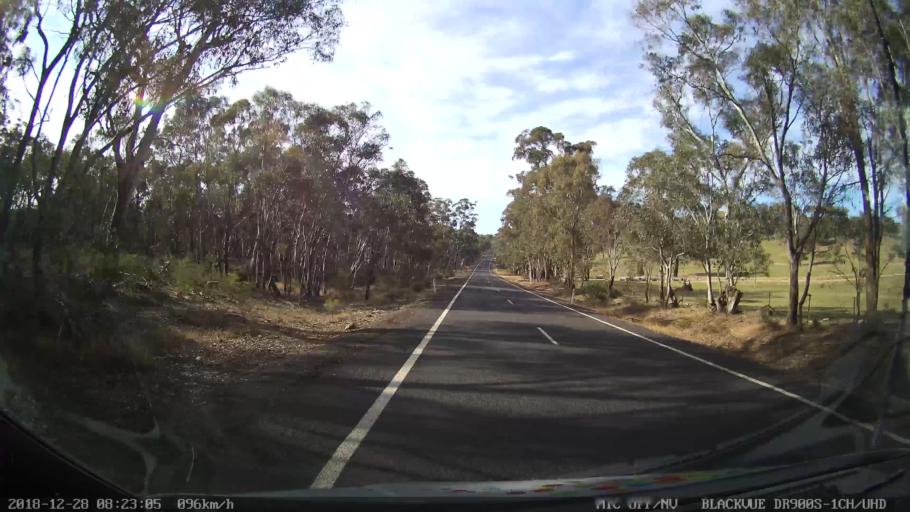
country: AU
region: New South Wales
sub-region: Blayney
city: Blayney
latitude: -33.9019
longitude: 149.3483
